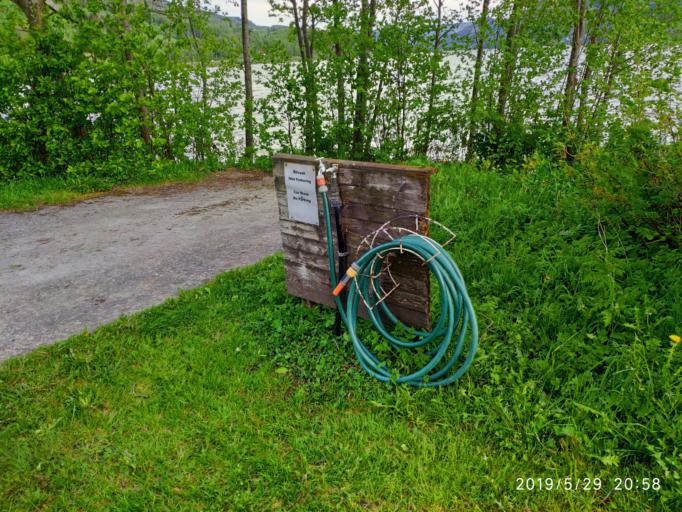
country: NO
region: Oppland
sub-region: Oyer
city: Tretten
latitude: 61.3662
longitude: 10.2834
